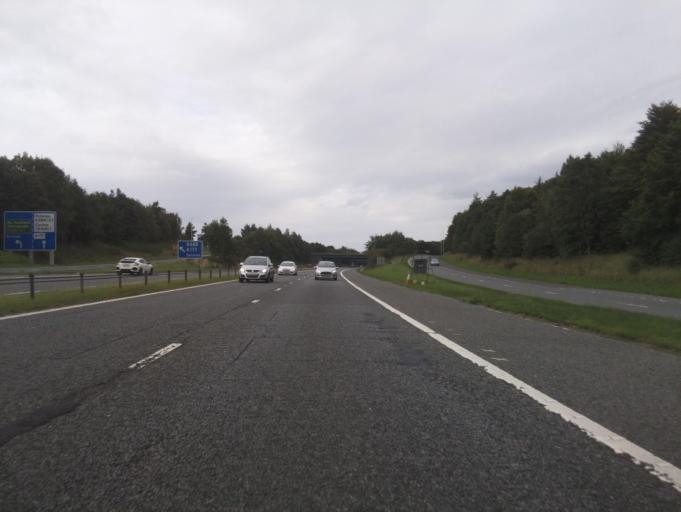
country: GB
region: England
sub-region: County Durham
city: Coxhoe
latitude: 54.7272
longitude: -1.5216
